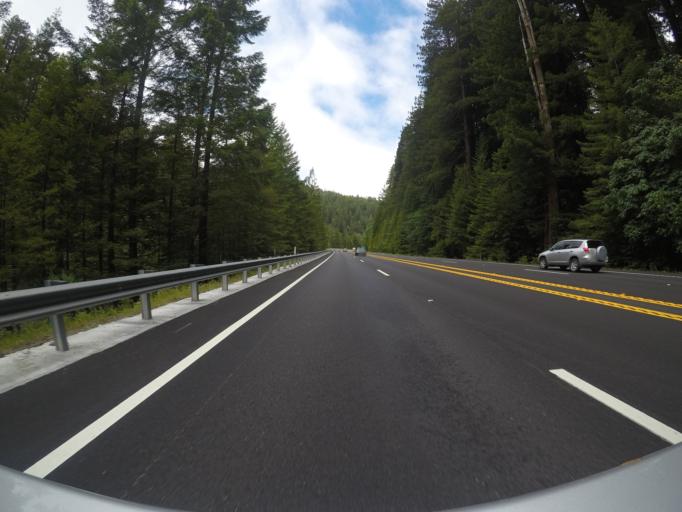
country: US
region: California
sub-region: Humboldt County
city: Rio Dell
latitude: 40.3488
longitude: -123.9301
